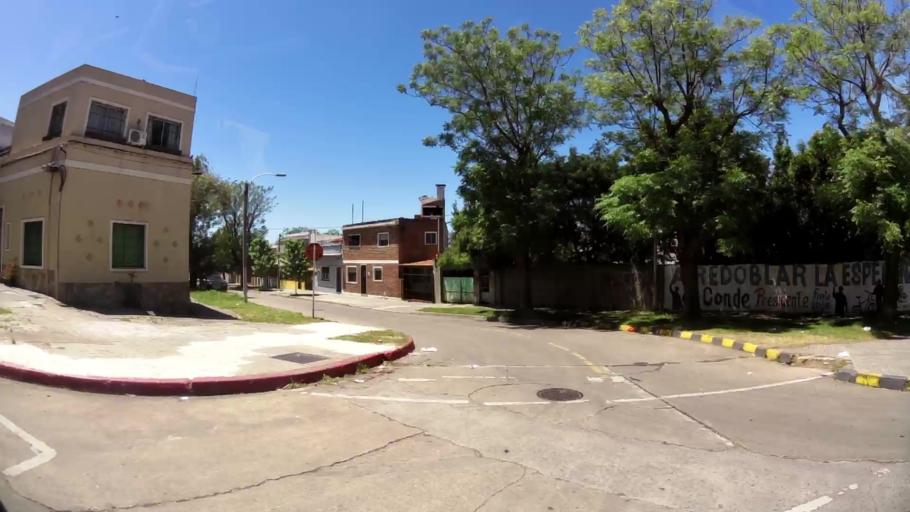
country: UY
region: Montevideo
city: Montevideo
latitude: -34.8981
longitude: -56.1363
